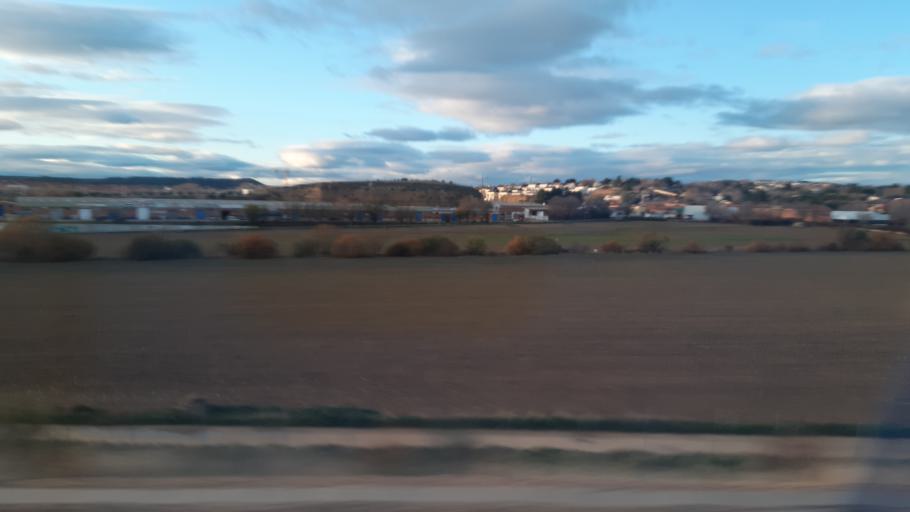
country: ES
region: Madrid
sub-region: Provincia de Madrid
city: Torres de la Alameda
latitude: 40.4365
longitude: -3.3513
